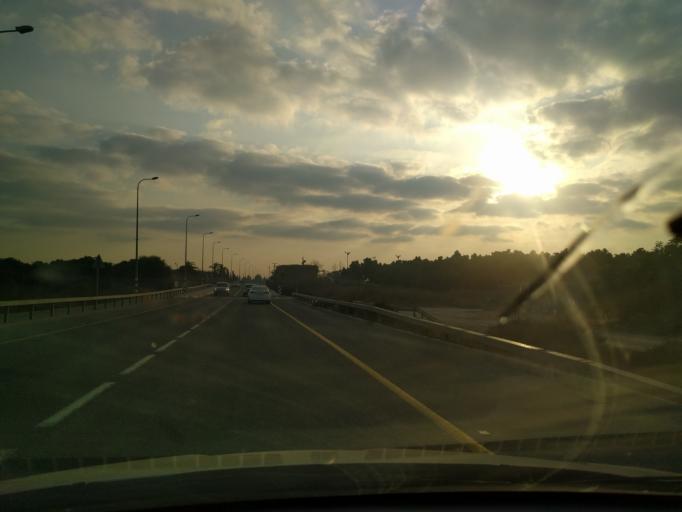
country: IL
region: Haifa
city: Qesarya
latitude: 32.5083
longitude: 34.9391
